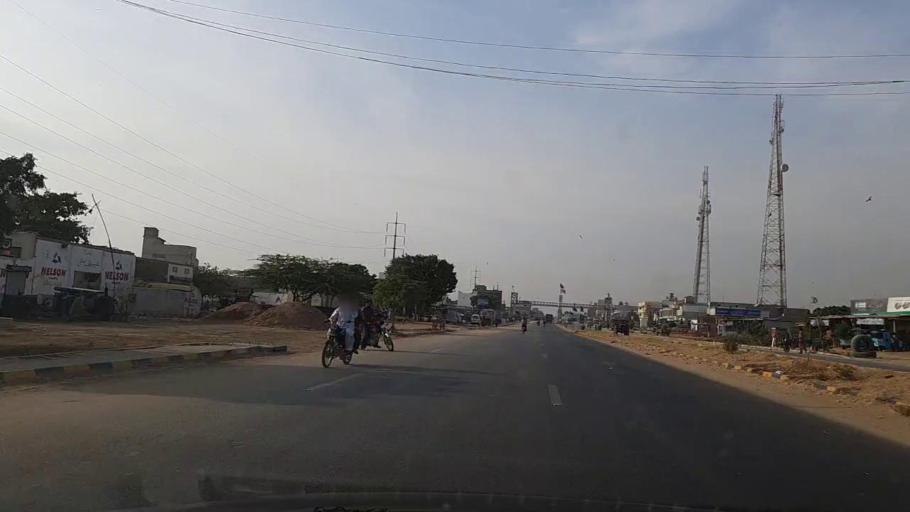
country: PK
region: Sindh
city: Gharo
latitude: 24.7881
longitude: 67.5284
